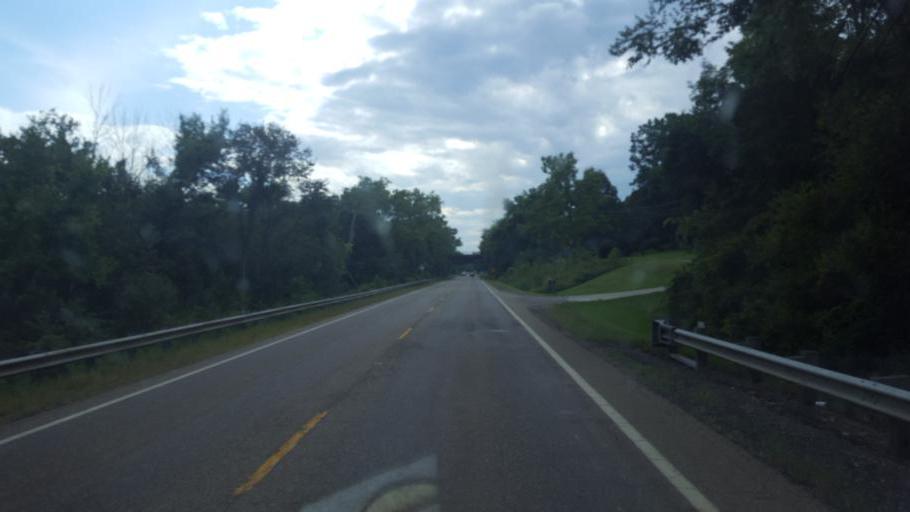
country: US
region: Ohio
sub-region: Tuscarawas County
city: Dover
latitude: 40.5860
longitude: -81.3829
